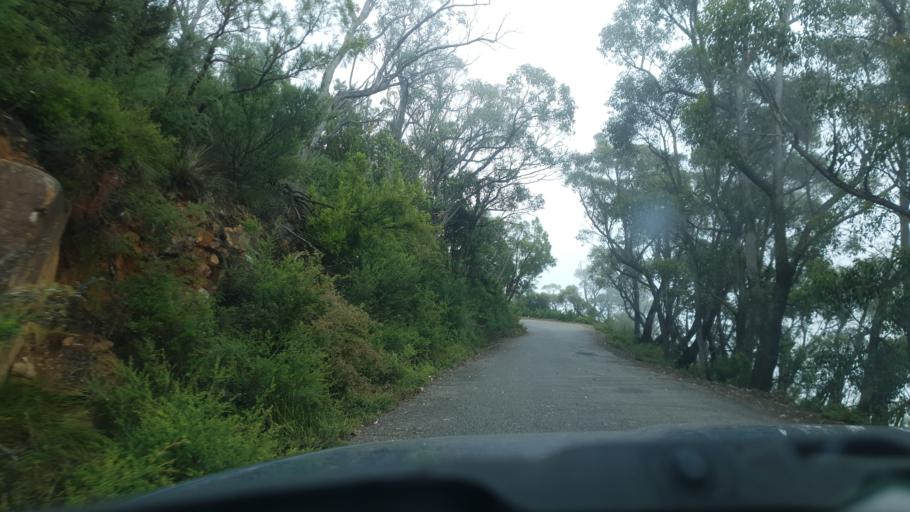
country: AU
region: Victoria
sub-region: Northern Grampians
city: Stawell
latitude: -37.2776
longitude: 142.5829
